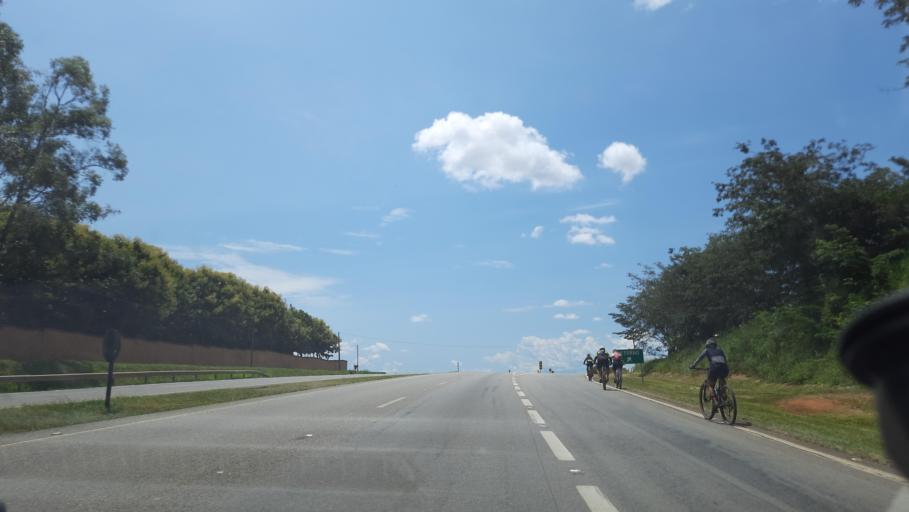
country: BR
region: Sao Paulo
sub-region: Mococa
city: Mococa
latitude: -21.5227
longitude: -47.0278
